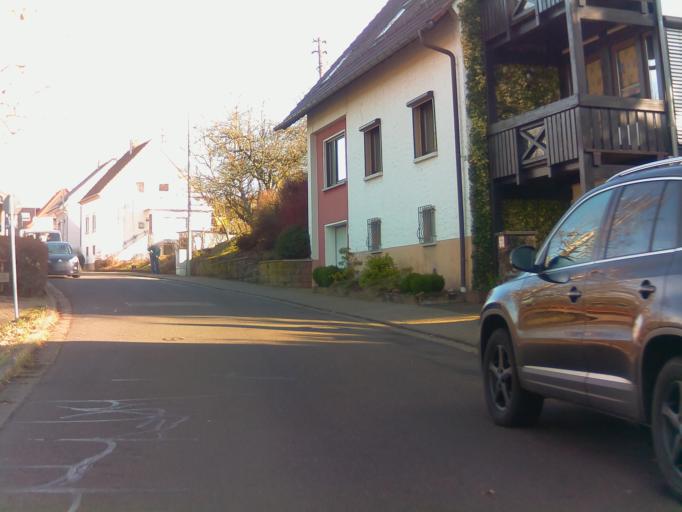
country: DE
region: Rheinland-Pfalz
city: Herschweiler-Pettersheim
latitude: 49.4785
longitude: 7.3489
